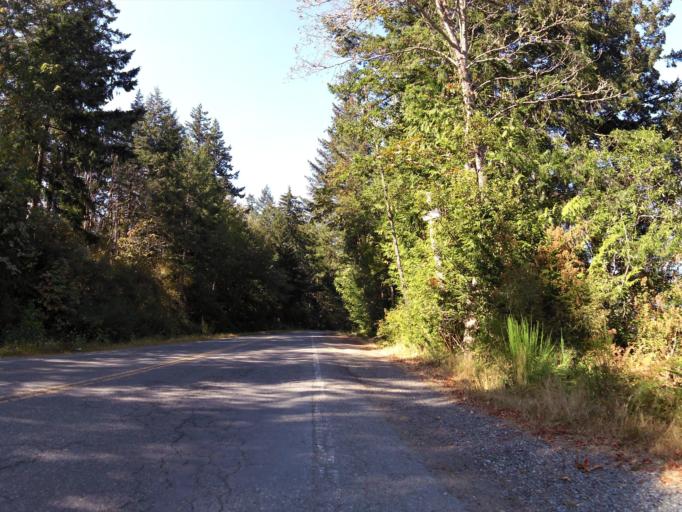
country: CA
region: British Columbia
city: North Saanich
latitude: 48.6287
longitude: -123.5294
